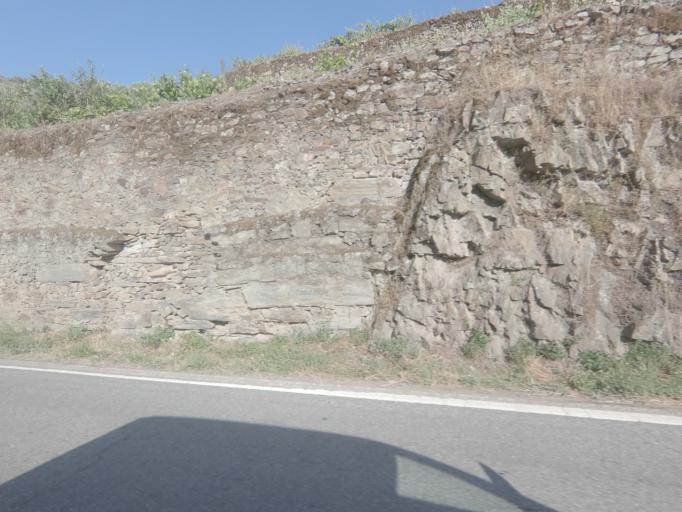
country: PT
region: Viseu
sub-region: Tabuaco
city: Tabuaco
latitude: 41.1792
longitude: -7.5506
